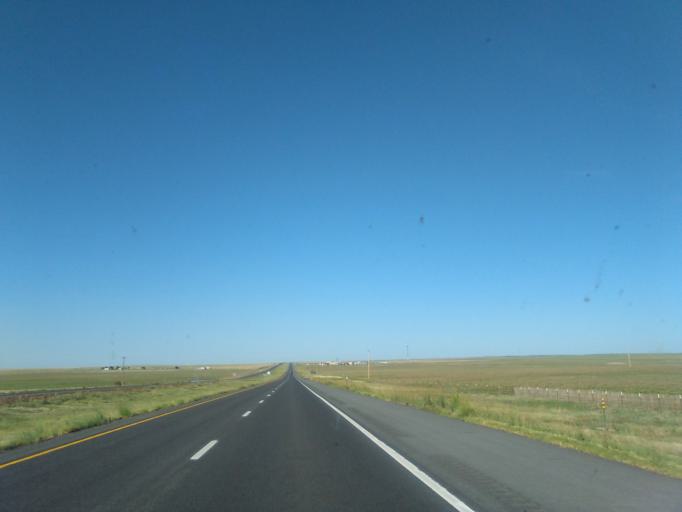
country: US
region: New Mexico
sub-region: San Miguel County
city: Las Vegas
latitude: 35.6876
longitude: -105.1401
